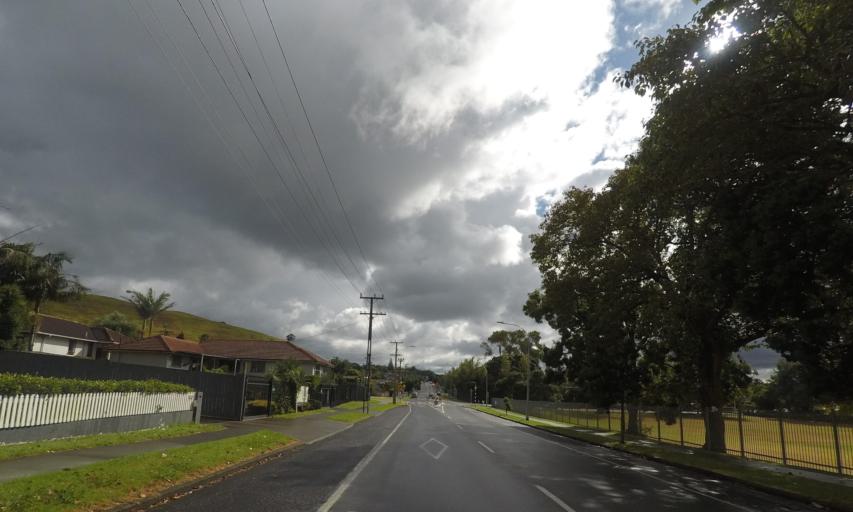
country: NZ
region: Auckland
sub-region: Auckland
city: Mangere
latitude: -36.9561
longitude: 174.7847
